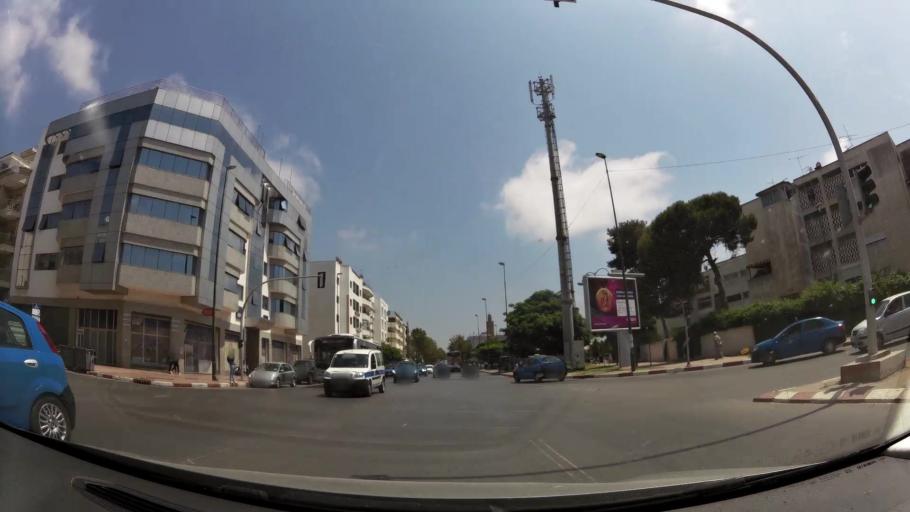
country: MA
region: Rabat-Sale-Zemmour-Zaer
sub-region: Rabat
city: Rabat
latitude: 34.0038
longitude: -6.8517
